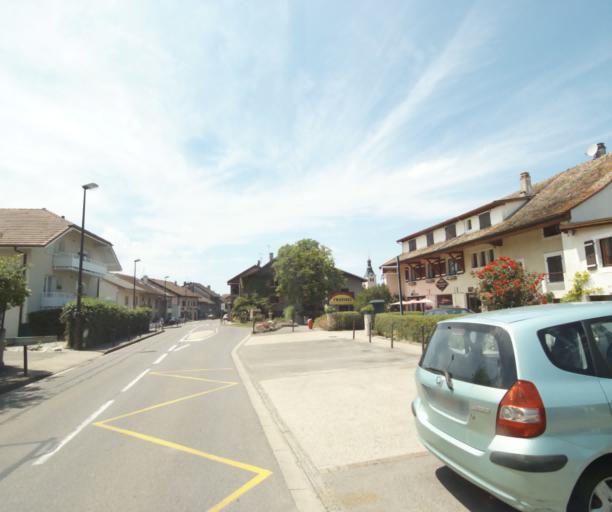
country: FR
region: Rhone-Alpes
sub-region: Departement de la Haute-Savoie
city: Messery
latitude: 46.3515
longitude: 6.2966
